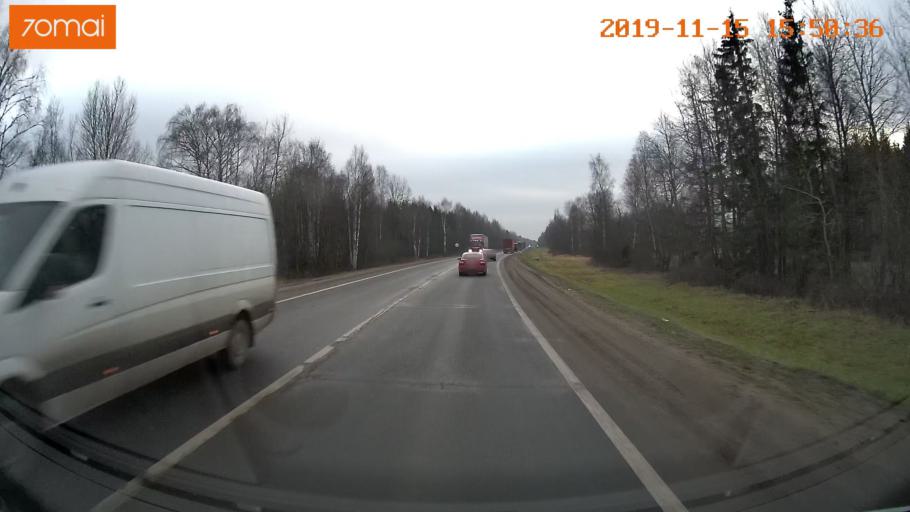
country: RU
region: Jaroslavl
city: Yaroslavl
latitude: 57.9040
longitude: 40.0133
